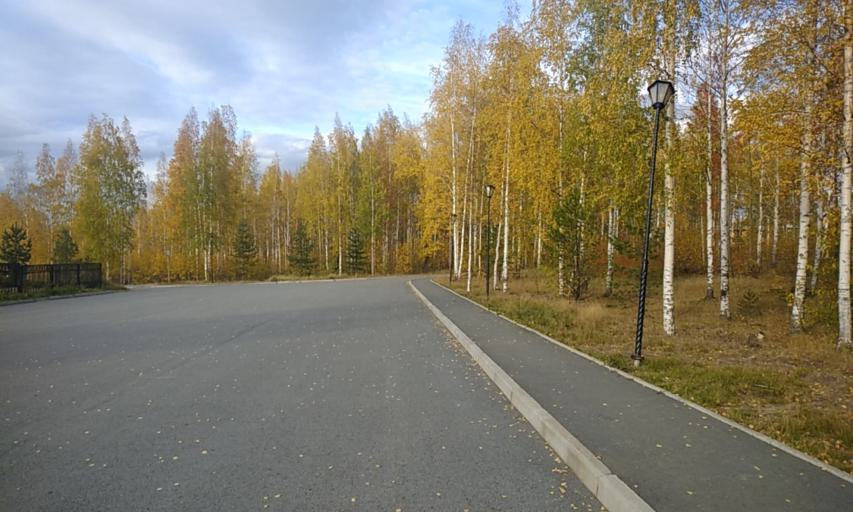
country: RU
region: Sverdlovsk
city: Krasnoural'sk
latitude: 58.3549
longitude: 60.0535
